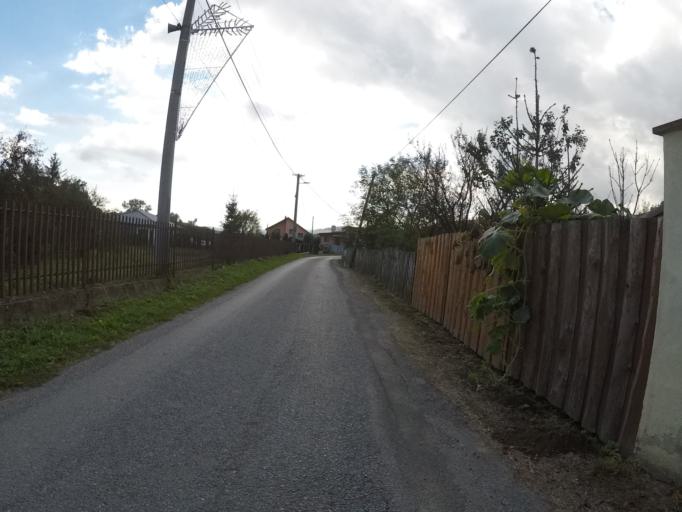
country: SK
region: Presovsky
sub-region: Okres Presov
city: Presov
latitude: 48.9383
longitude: 21.1794
